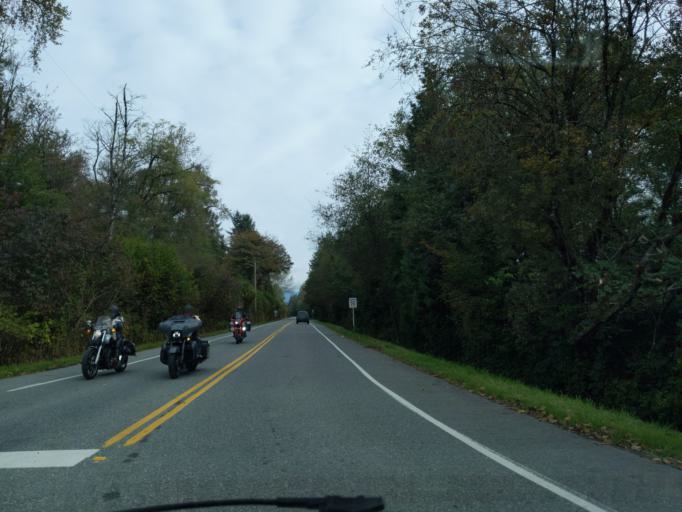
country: CA
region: British Columbia
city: Walnut Grove
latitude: 49.1975
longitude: -122.6443
